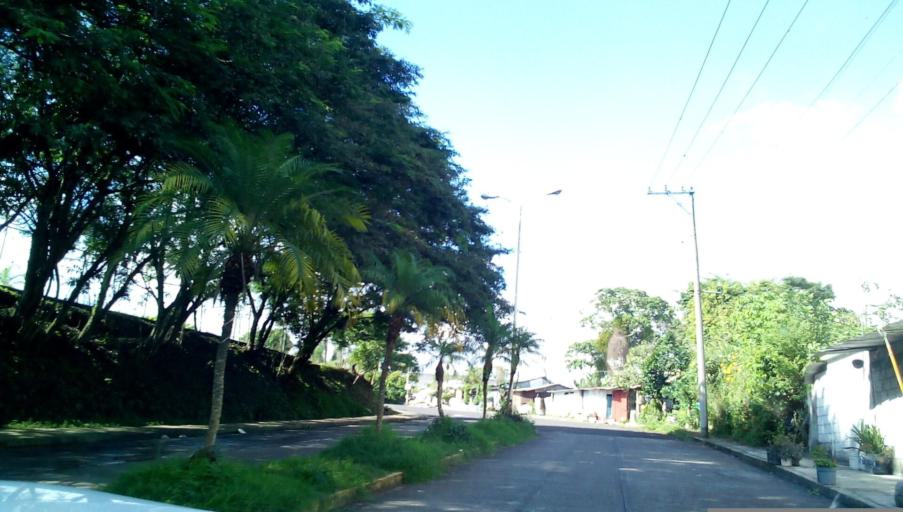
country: MX
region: Veracruz
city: Cordoba
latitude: 18.8916
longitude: -96.9204
